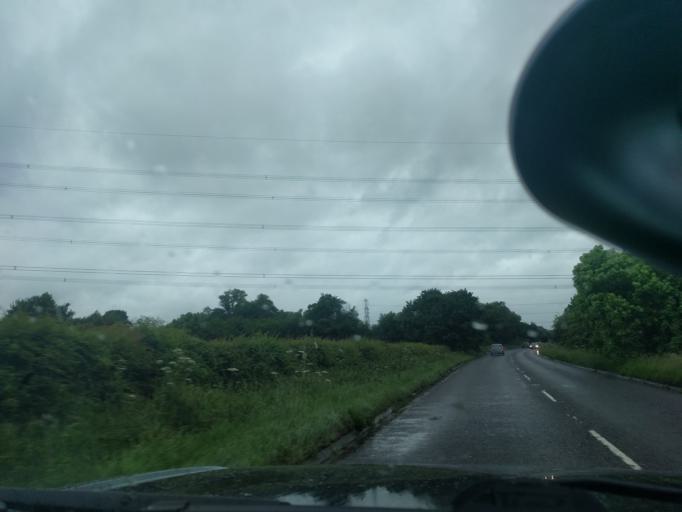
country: GB
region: England
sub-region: Wiltshire
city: Corsham
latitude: 51.4464
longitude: -2.1569
